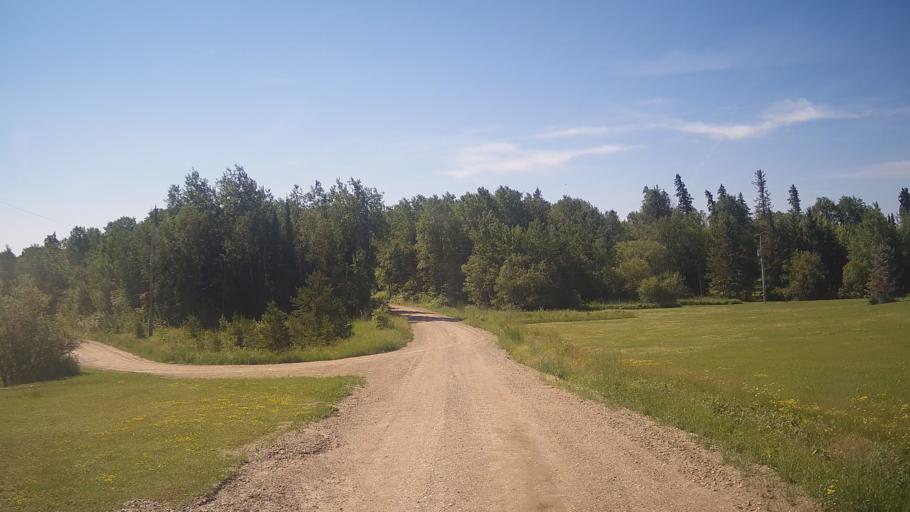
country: CA
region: Ontario
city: Dryden
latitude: 49.8223
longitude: -93.3389
